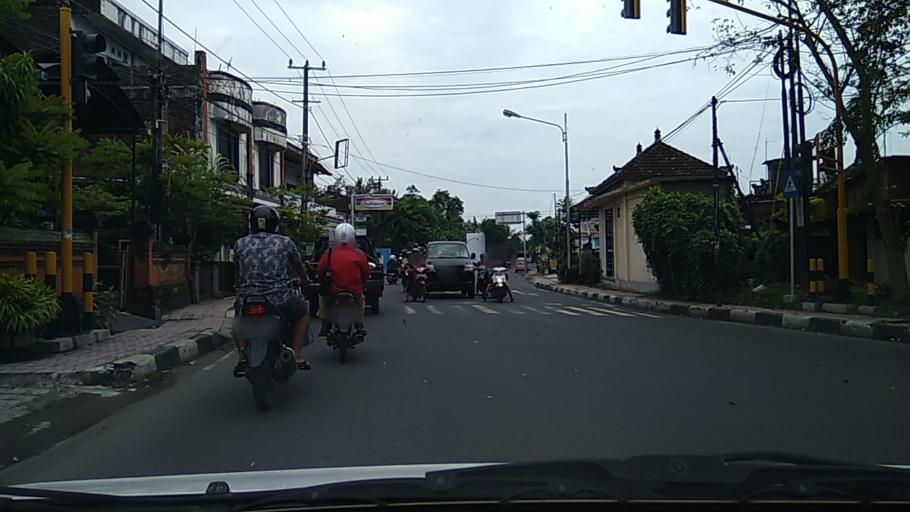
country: ID
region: Bali
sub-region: Kabupaten Gianyar
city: Ubud
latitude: -8.5331
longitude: 115.3028
